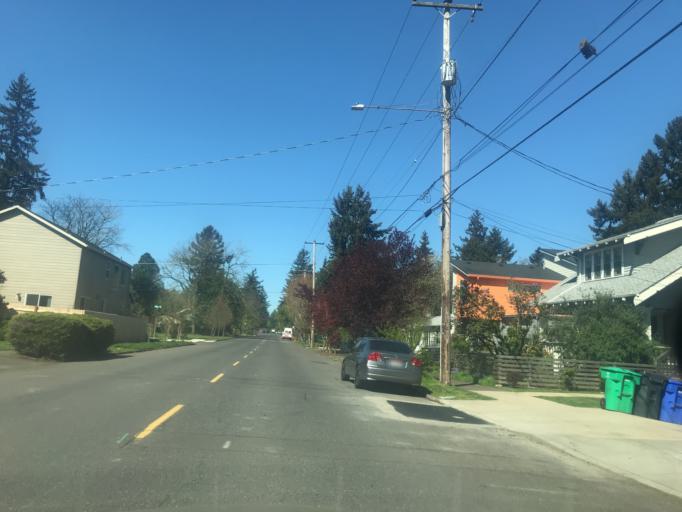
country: US
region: Oregon
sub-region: Multnomah County
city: Lents
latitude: 45.4831
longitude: -122.6001
